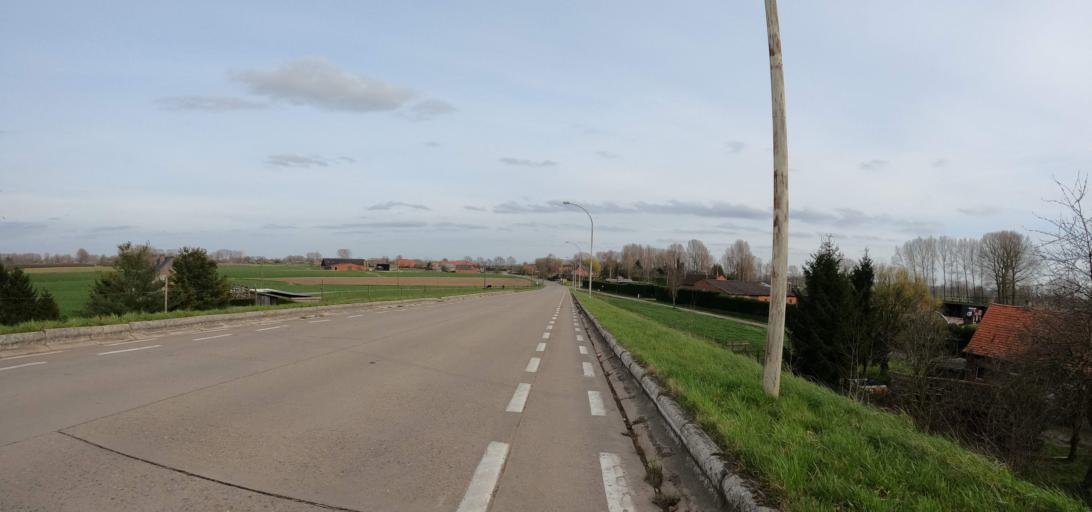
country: BE
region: Flanders
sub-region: Provincie Oost-Vlaanderen
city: Beveren
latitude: 51.1708
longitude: 4.2574
